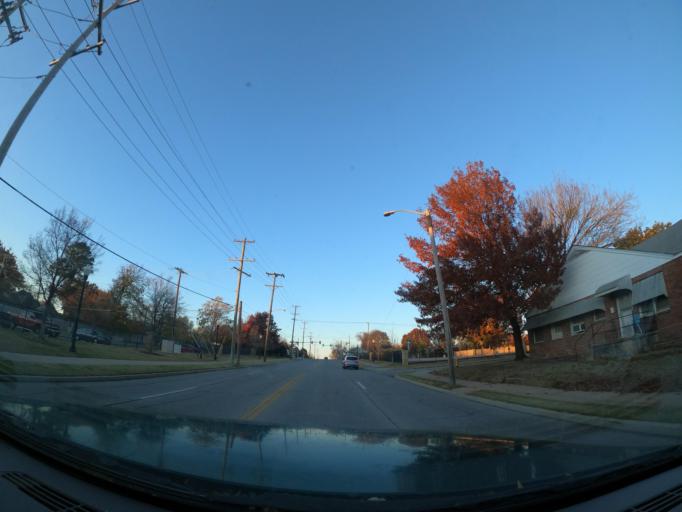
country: US
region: Oklahoma
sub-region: Tulsa County
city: Tulsa
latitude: 36.1548
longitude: -95.9403
